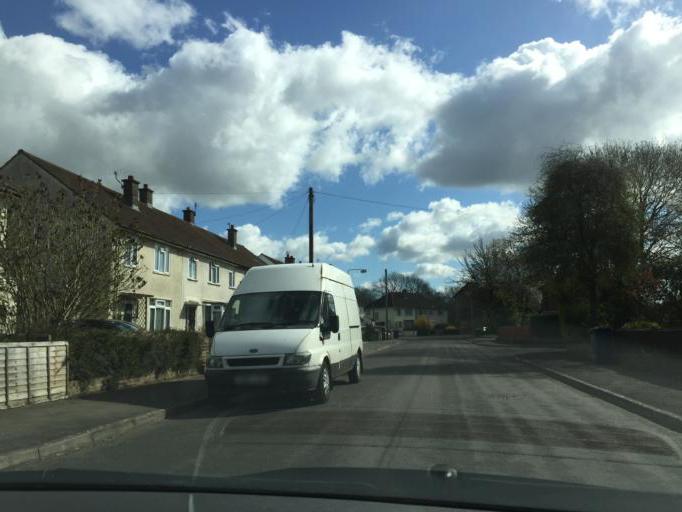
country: GB
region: England
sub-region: Oxfordshire
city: Oxford
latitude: 51.7715
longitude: -1.2236
